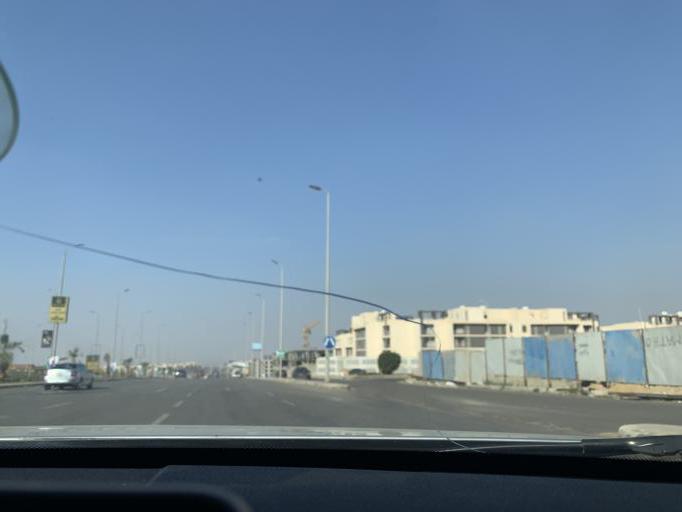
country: EG
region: Muhafazat al Qalyubiyah
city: Al Khankah
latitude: 30.0179
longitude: 31.4750
